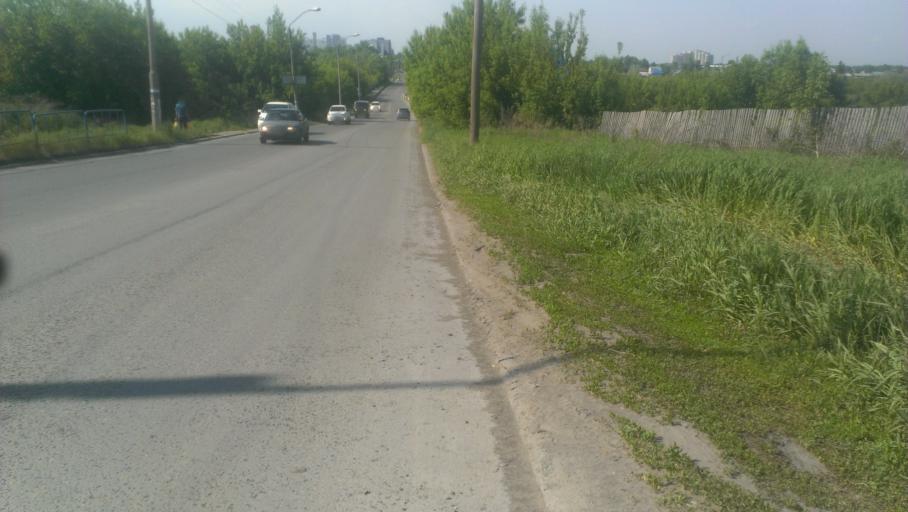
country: RU
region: Altai Krai
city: Novoaltaysk
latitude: 53.4025
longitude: 83.9461
